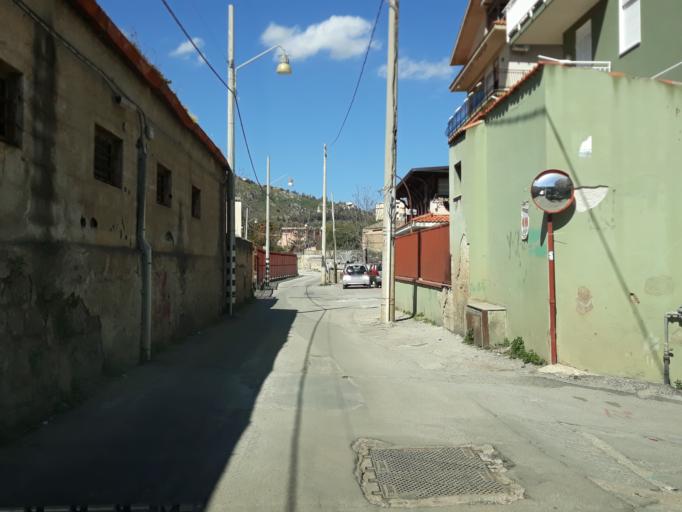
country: IT
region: Sicily
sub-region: Palermo
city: Villa Ciambra
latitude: 38.0899
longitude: 13.3217
